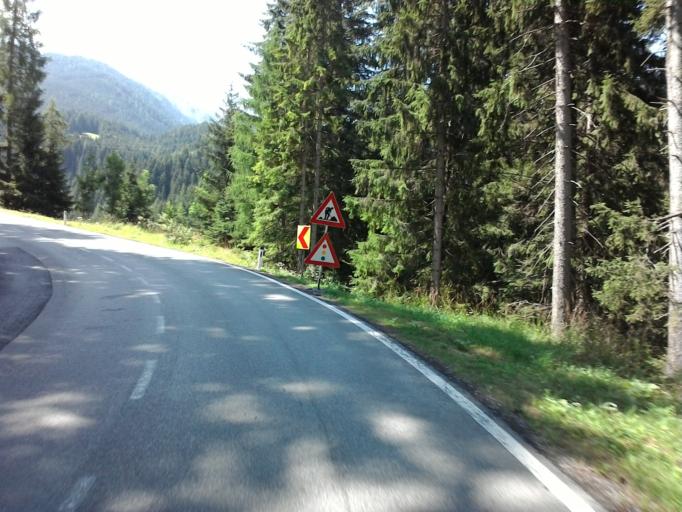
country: AT
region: Tyrol
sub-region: Politischer Bezirk Lienz
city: Heinfels
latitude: 46.7412
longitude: 12.4677
